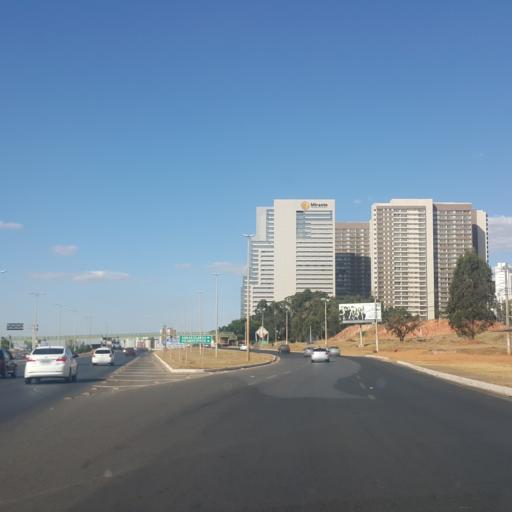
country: BR
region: Federal District
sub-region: Brasilia
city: Brasilia
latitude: -15.8314
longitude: -48.0464
